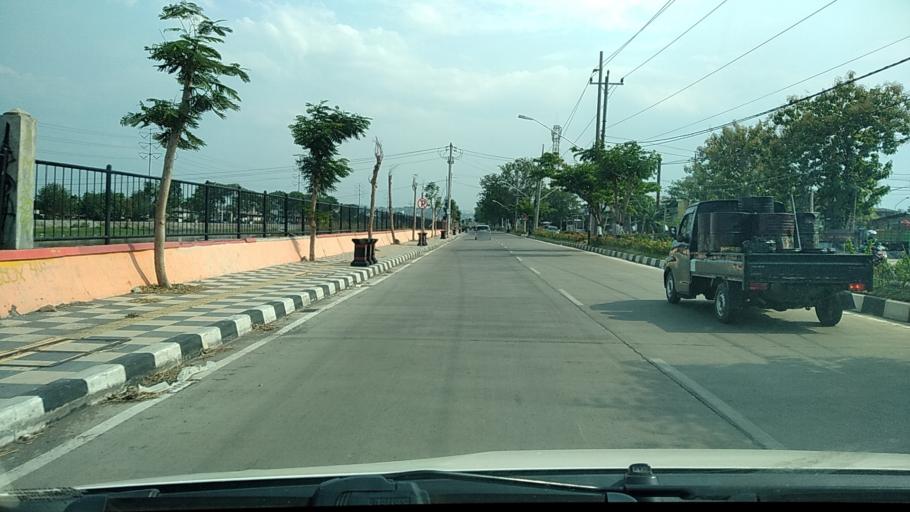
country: ID
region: Central Java
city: Semarang
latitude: -6.9721
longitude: 110.4005
